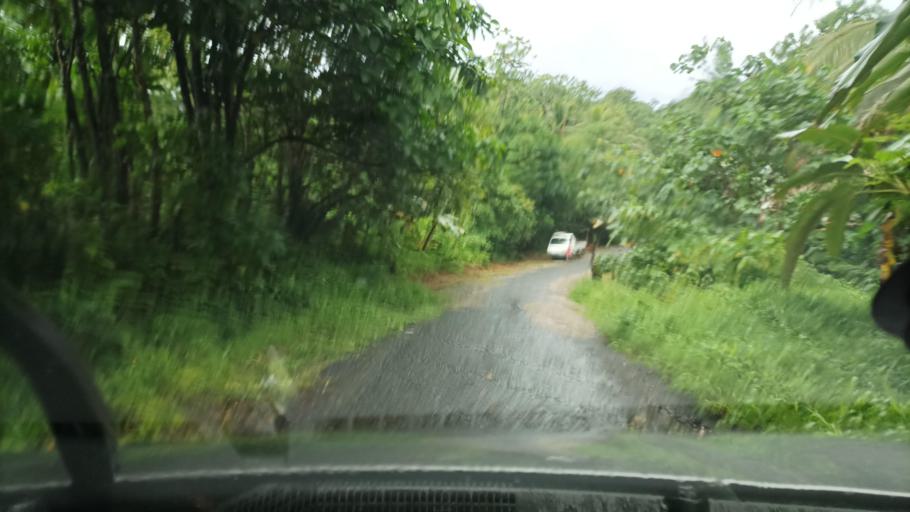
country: FM
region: Pohnpei
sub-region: Sokehs Municipality
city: Palikir - National Government Center
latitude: 6.8408
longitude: 158.1773
